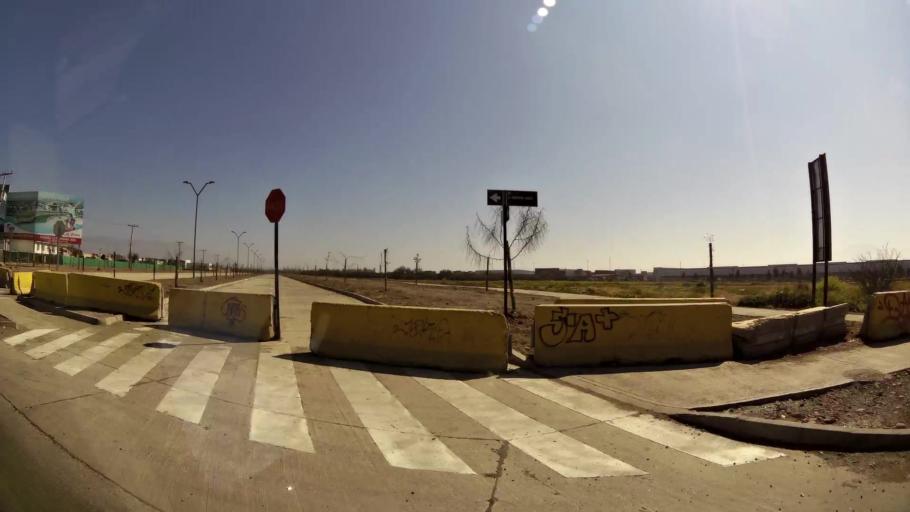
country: CL
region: Santiago Metropolitan
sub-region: Provincia de Chacabuco
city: Chicureo Abajo
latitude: -33.3242
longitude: -70.7432
